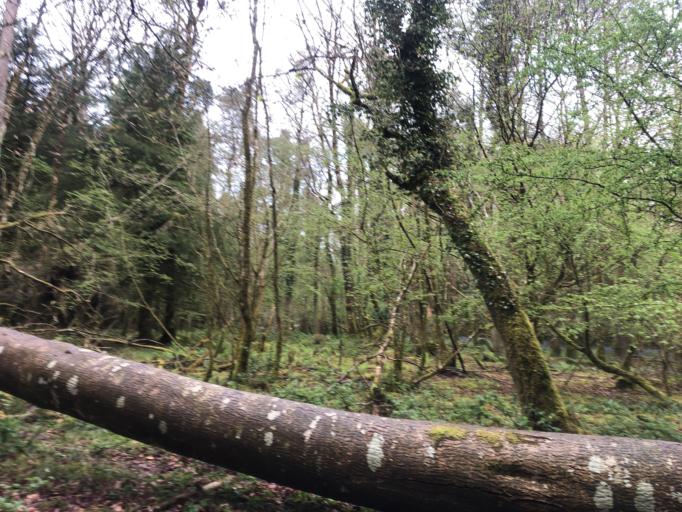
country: IE
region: Connaught
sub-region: Roscommon
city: Boyle
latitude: 53.9843
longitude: -8.1973
